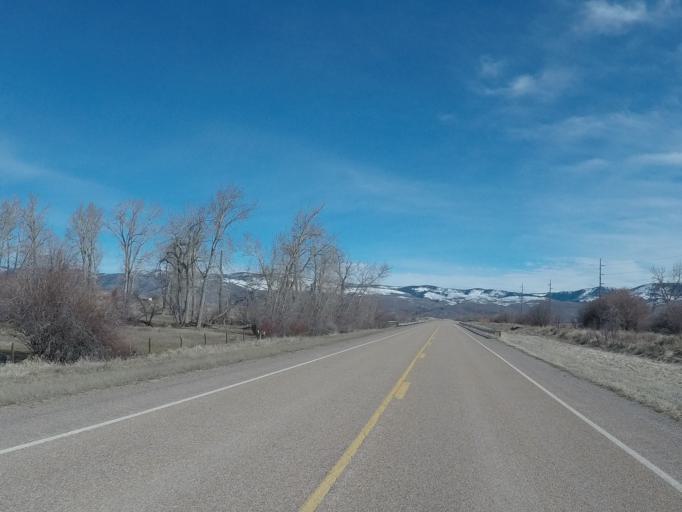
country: US
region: Montana
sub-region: Granite County
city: Philipsburg
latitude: 46.6125
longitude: -113.1783
